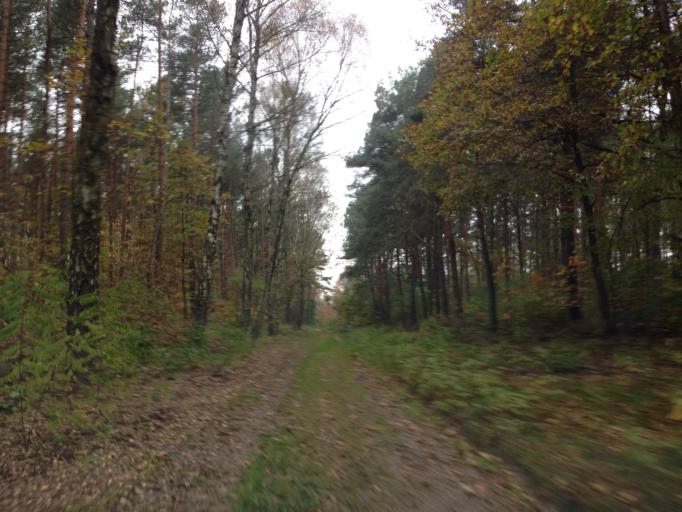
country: PL
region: Masovian Voivodeship
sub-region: Powiat warszawski zachodni
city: Leszno
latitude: 52.2738
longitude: 20.5992
